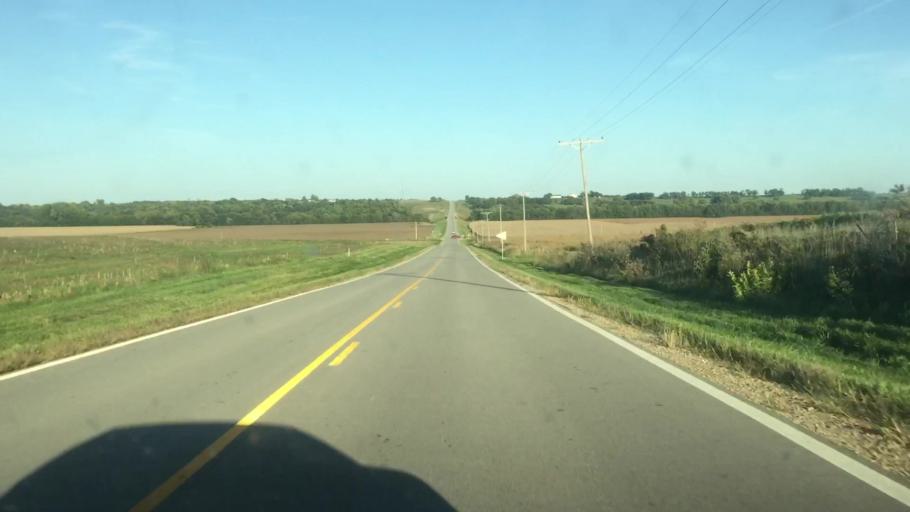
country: US
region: Kansas
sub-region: Brown County
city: Horton
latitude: 39.5875
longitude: -95.5697
